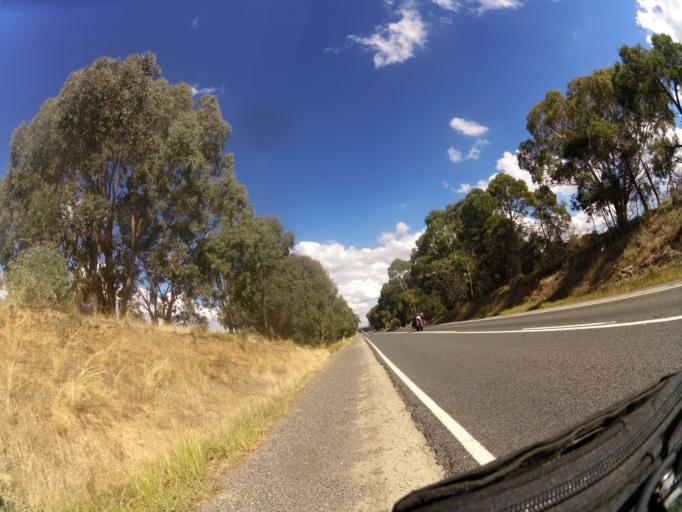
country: AU
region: Victoria
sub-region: Mansfield
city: Mansfield
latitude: -36.8868
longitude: 145.9951
